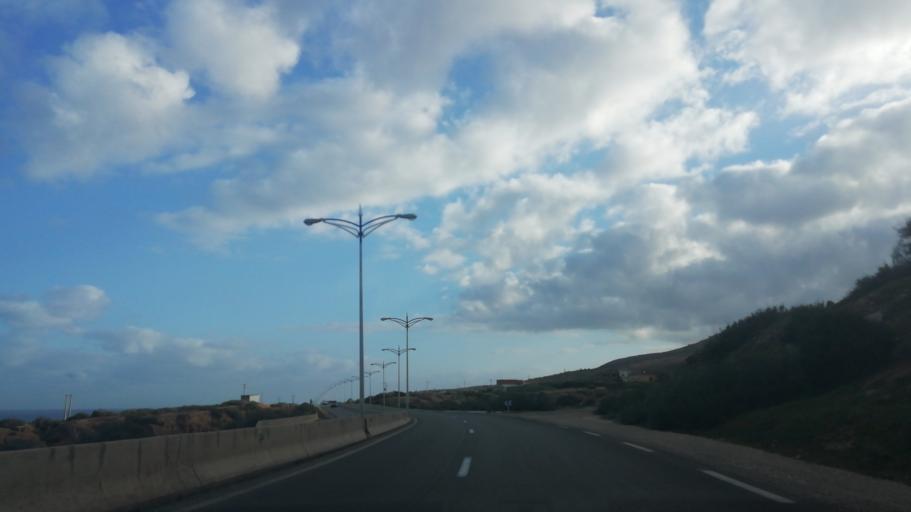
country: DZ
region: Mostaganem
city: Mostaganem
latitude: 36.0570
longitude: 0.1627
